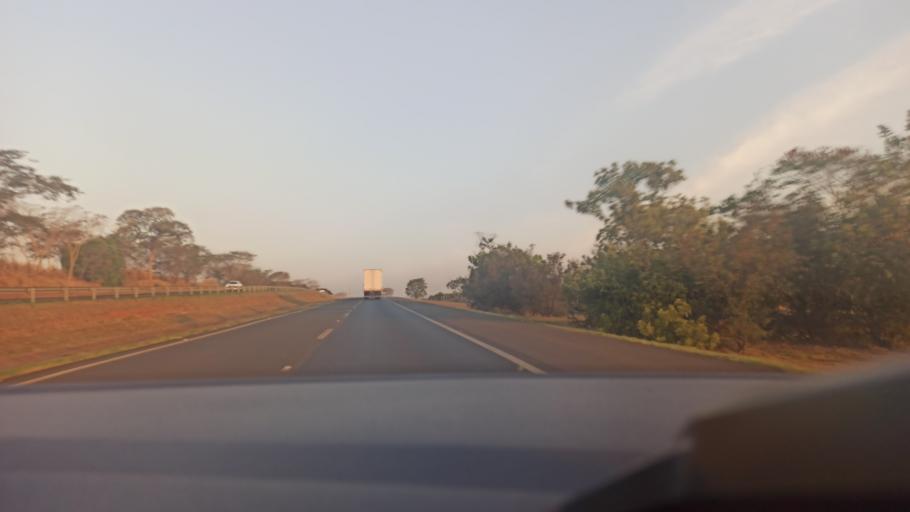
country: BR
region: Sao Paulo
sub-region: Santa Adelia
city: Santa Adelia
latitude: -21.4010
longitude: -48.7065
